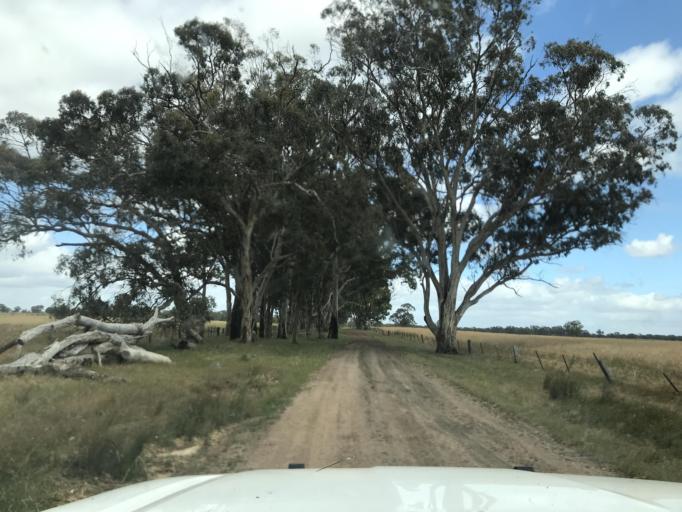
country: AU
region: South Australia
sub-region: Naracoorte and Lucindale
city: Naracoorte
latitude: -36.8985
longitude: 141.3820
